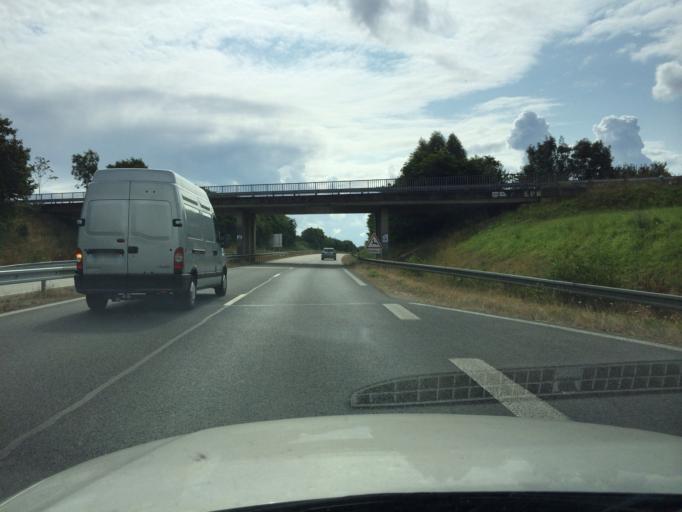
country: FR
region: Lower Normandy
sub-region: Departement de la Manche
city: Montebourg
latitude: 49.4921
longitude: -1.4075
